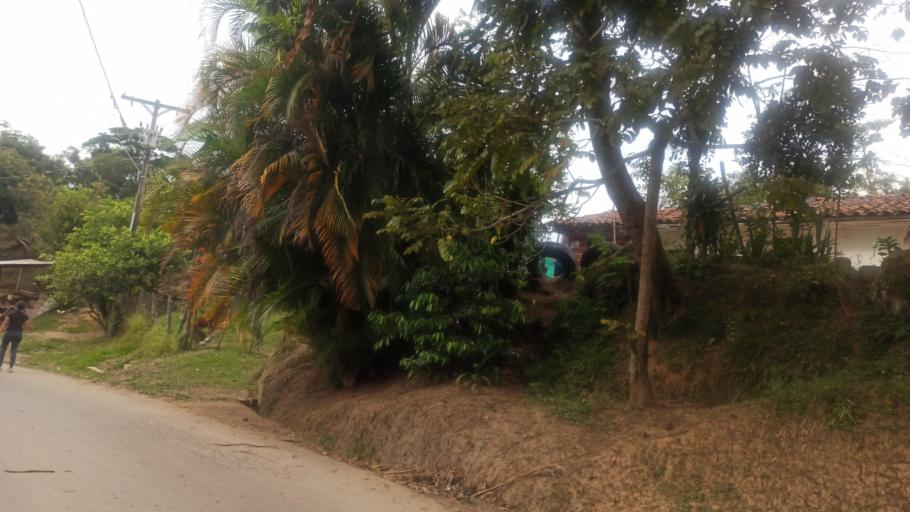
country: CO
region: Valle del Cauca
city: Jamundi
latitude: 3.2070
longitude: -76.6309
